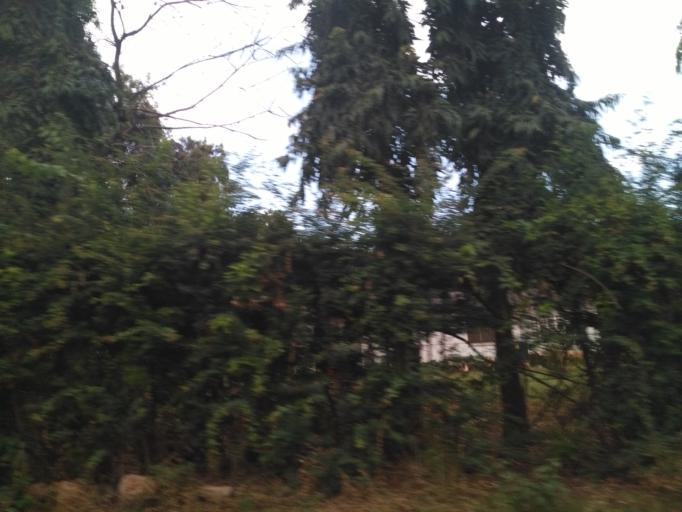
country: TZ
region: Dar es Salaam
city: Magomeni
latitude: -6.7698
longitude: 39.2729
